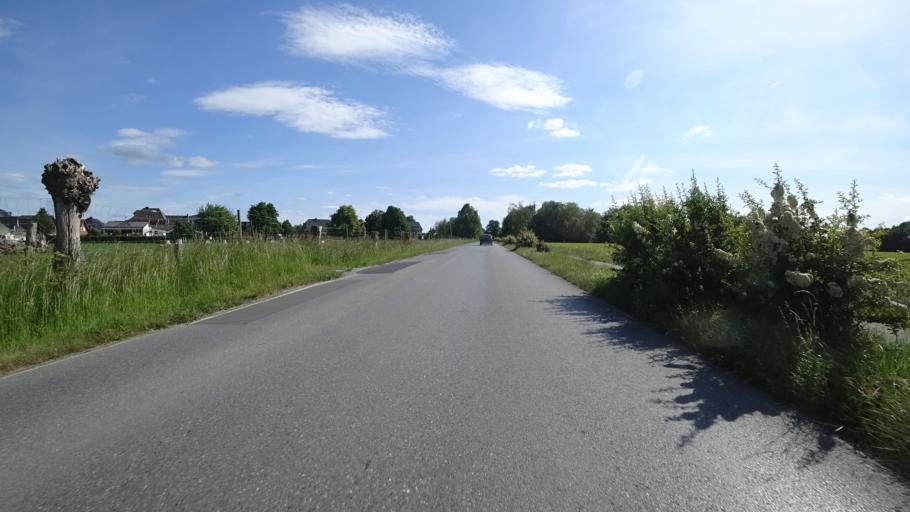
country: DE
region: North Rhine-Westphalia
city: Erwitte
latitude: 51.6273
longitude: 8.3579
